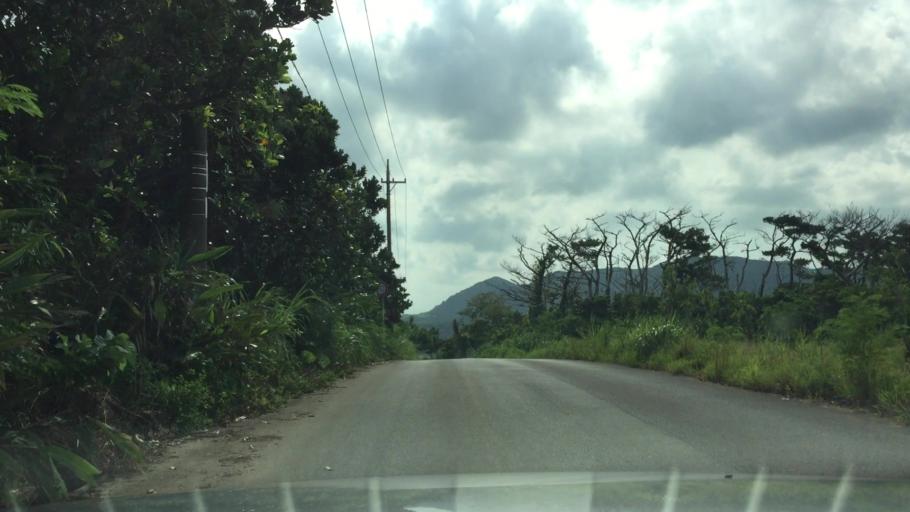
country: JP
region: Okinawa
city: Ishigaki
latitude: 24.4013
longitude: 124.2116
